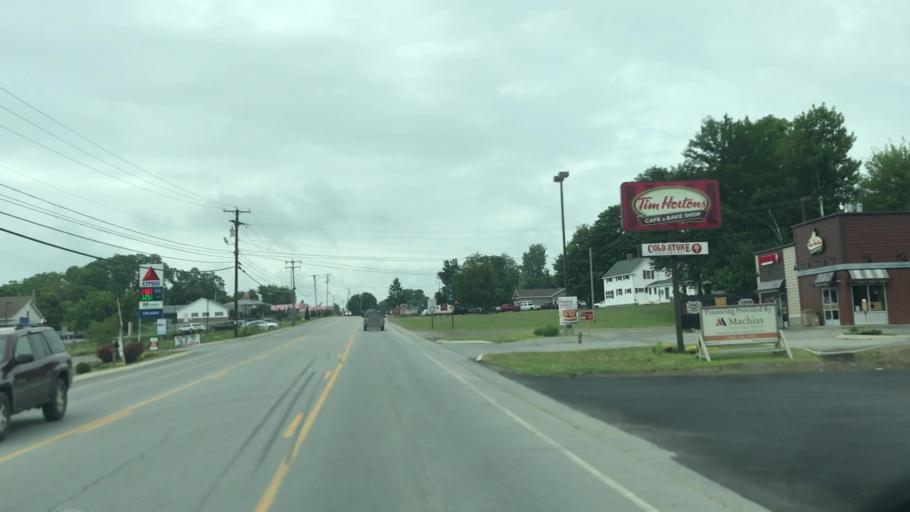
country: US
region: Maine
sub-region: Penobscot County
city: Lincoln
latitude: 45.3591
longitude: -68.5229
